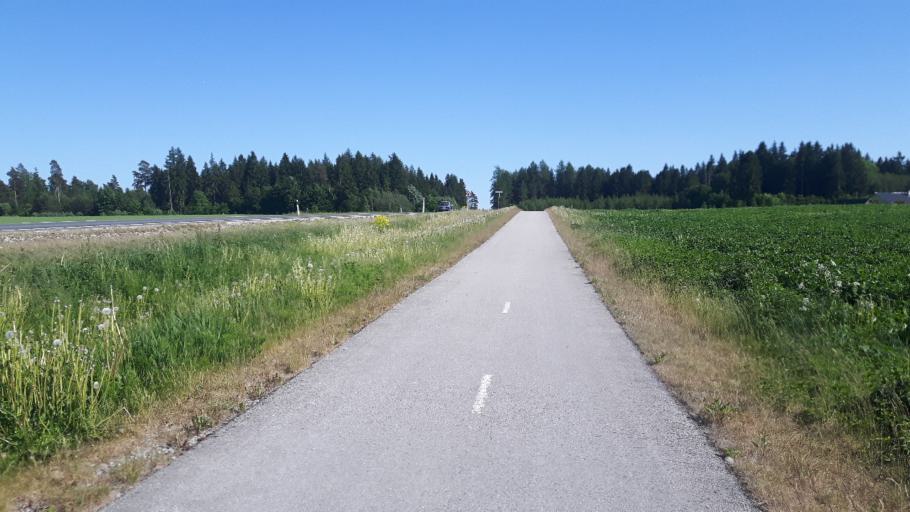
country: EE
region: Raplamaa
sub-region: Kehtna vald
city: Kehtna
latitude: 58.9635
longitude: 24.8585
